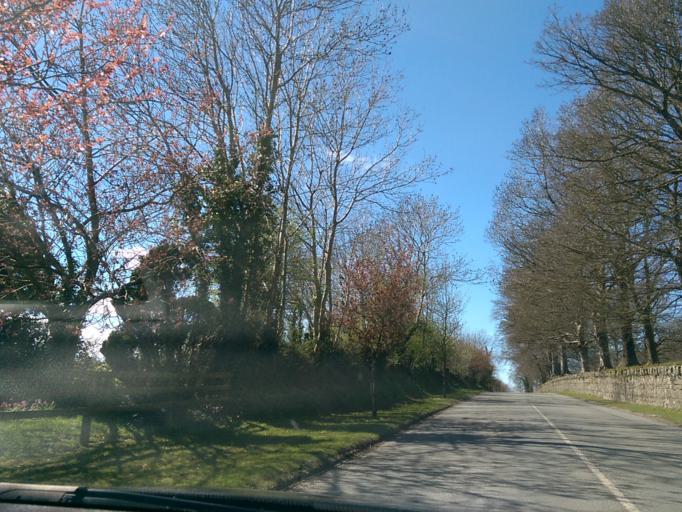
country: IE
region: Leinster
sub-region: Wicklow
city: Baltinglass
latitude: 52.9062
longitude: -6.6122
